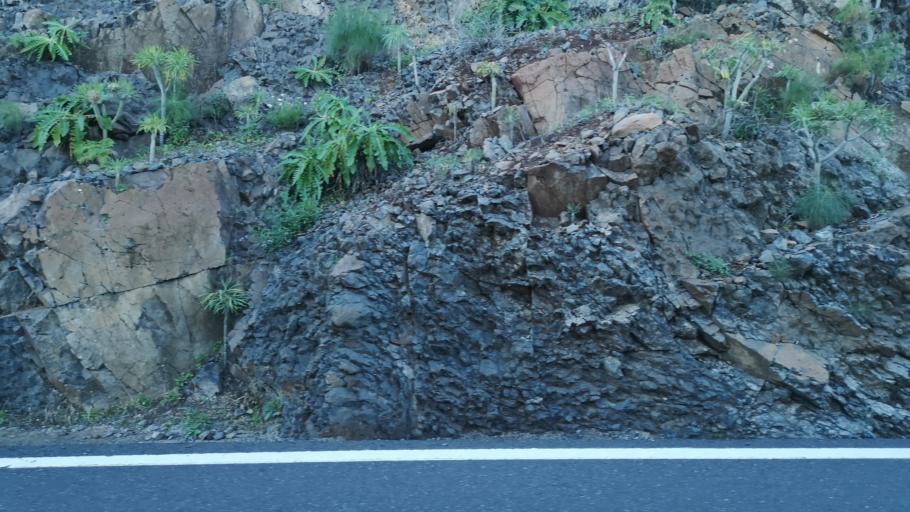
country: ES
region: Canary Islands
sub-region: Provincia de Santa Cruz de Tenerife
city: San Sebastian de la Gomera
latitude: 28.0839
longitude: -17.1326
